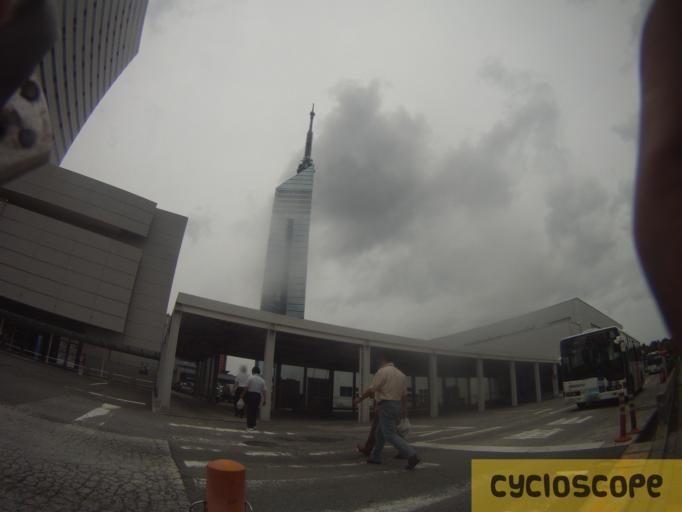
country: JP
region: Fukuoka
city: Fukuoka-shi
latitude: 33.5929
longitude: 130.3523
